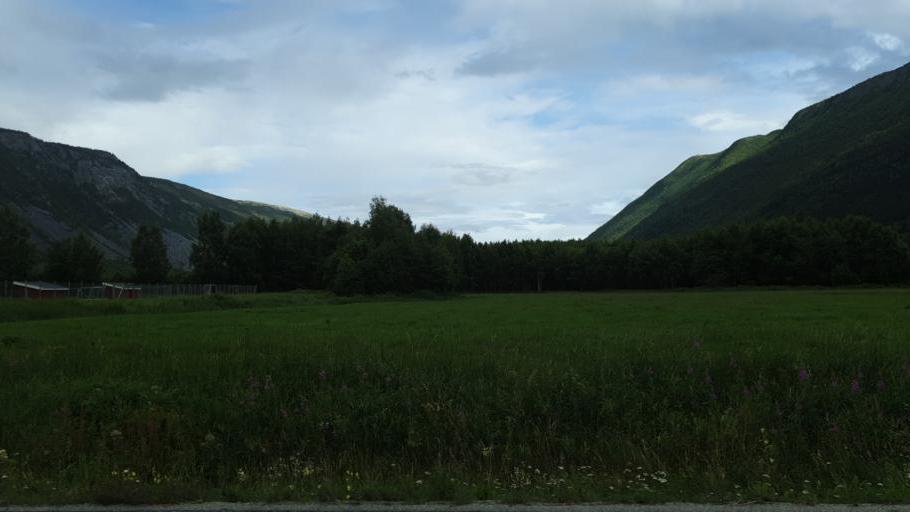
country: NO
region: Oppland
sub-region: Sel
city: Otta
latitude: 61.8436
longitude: 9.4133
